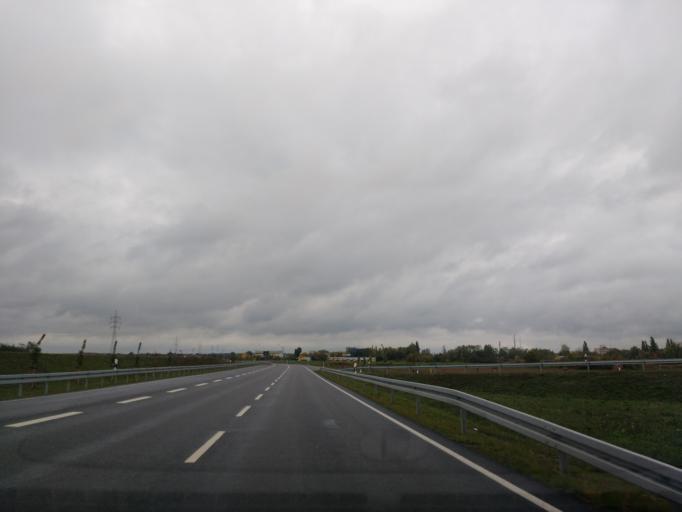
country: DE
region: Saxony-Anhalt
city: Halle (Saale)
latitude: 51.4953
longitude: 12.0157
